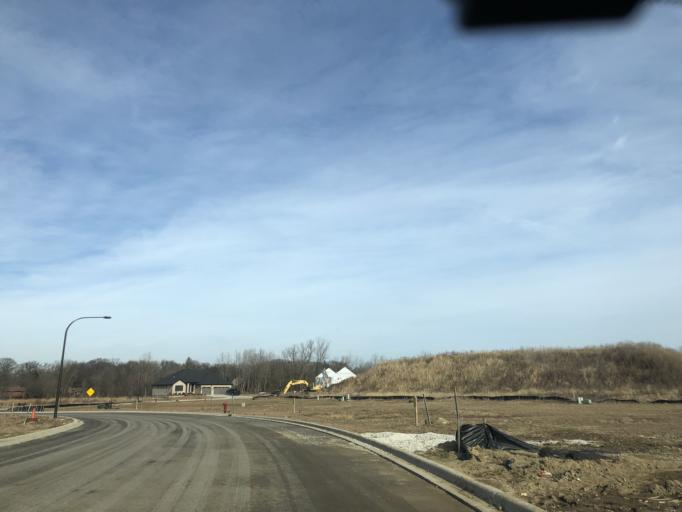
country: US
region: Illinois
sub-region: DuPage County
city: Woodridge
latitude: 41.7193
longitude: -88.0127
